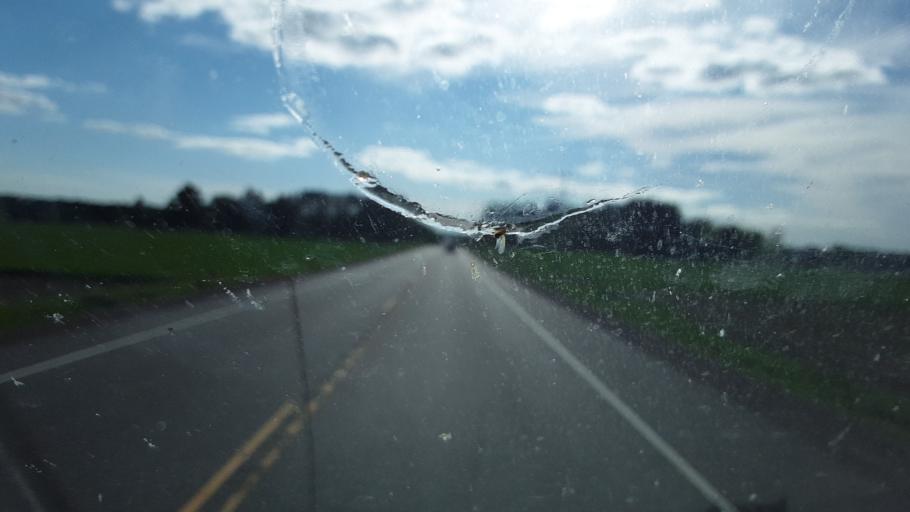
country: US
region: Wisconsin
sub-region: Wood County
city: Marshfield
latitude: 44.6557
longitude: -90.2051
